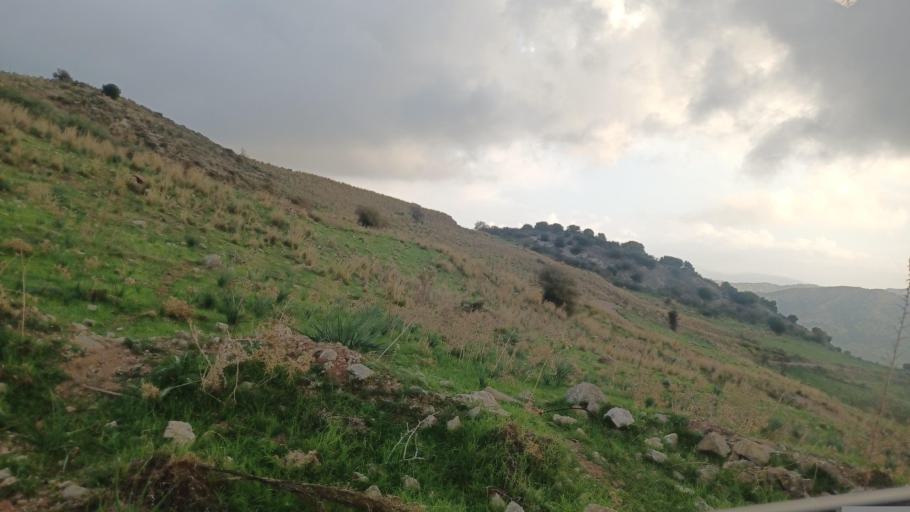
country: CY
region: Pafos
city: Mesogi
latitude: 34.7841
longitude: 32.5140
